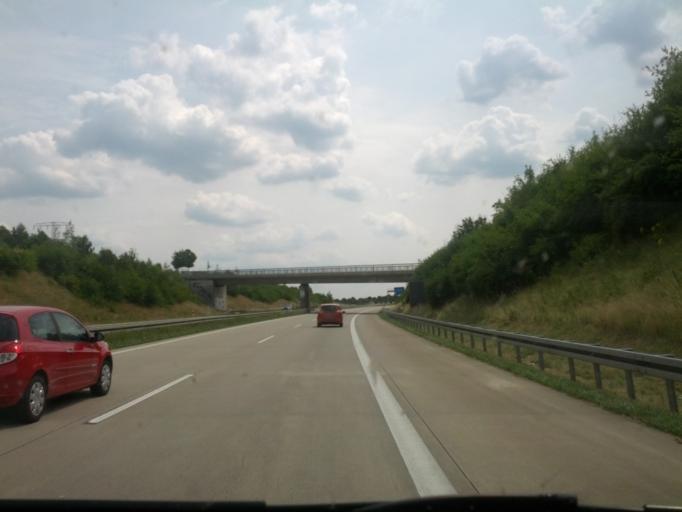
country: DE
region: Saxony
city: Dohna
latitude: 50.9572
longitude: 13.8669
